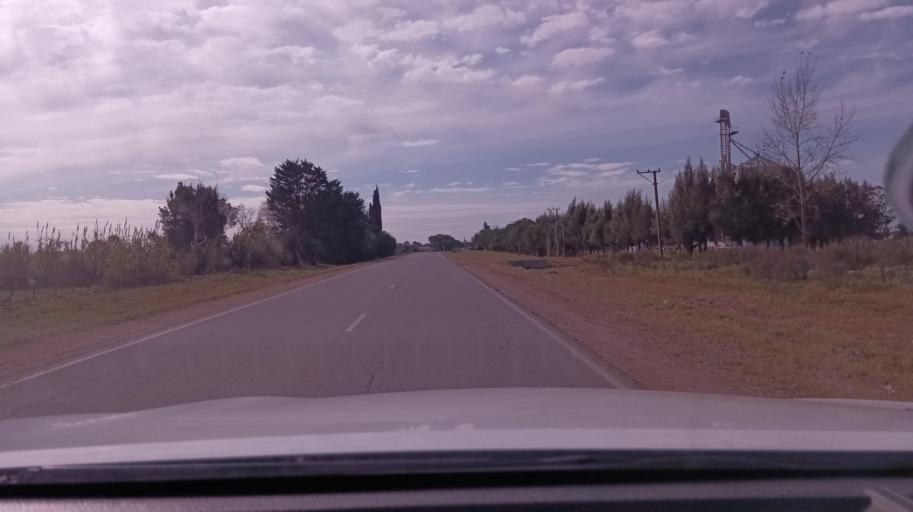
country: UY
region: Canelones
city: Toledo
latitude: -34.7319
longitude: -56.1140
